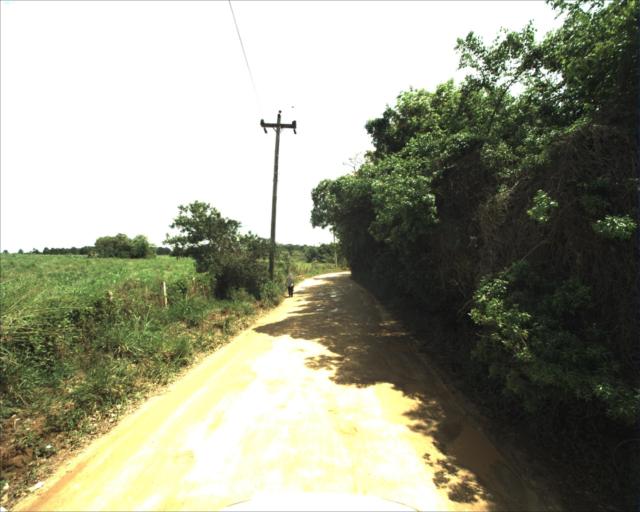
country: BR
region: Sao Paulo
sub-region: Aracoiaba Da Serra
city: Aracoiaba da Serra
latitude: -23.5564
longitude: -47.5523
